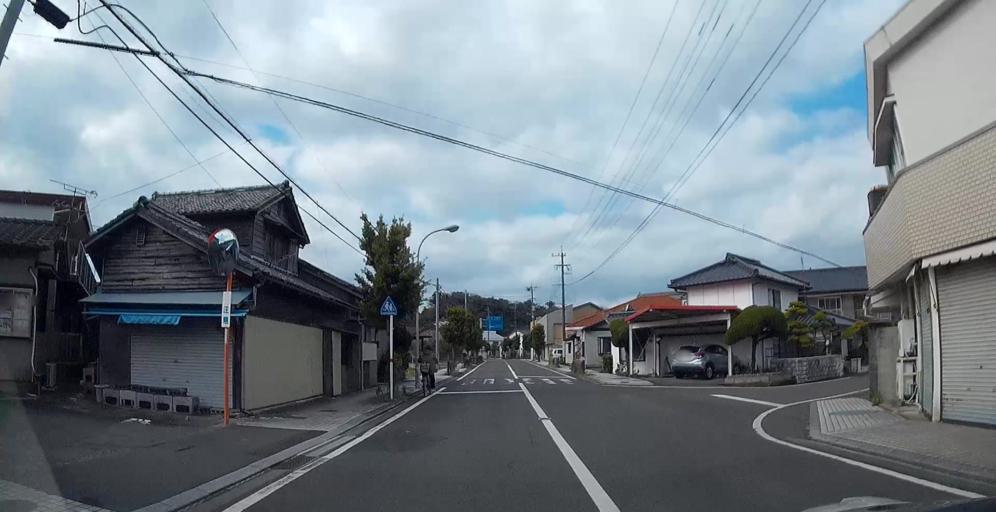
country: JP
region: Kumamoto
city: Minamata
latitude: 32.2120
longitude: 130.3893
